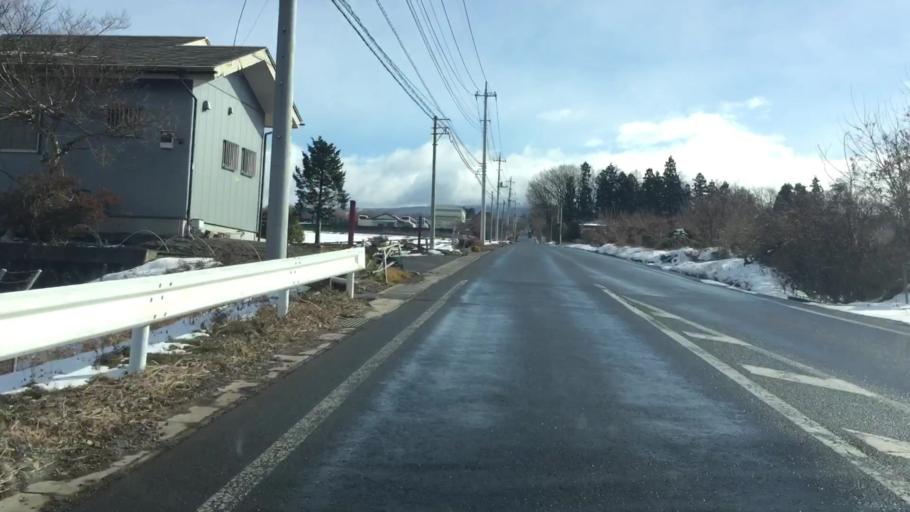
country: JP
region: Gunma
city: Numata
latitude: 36.6101
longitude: 139.0796
